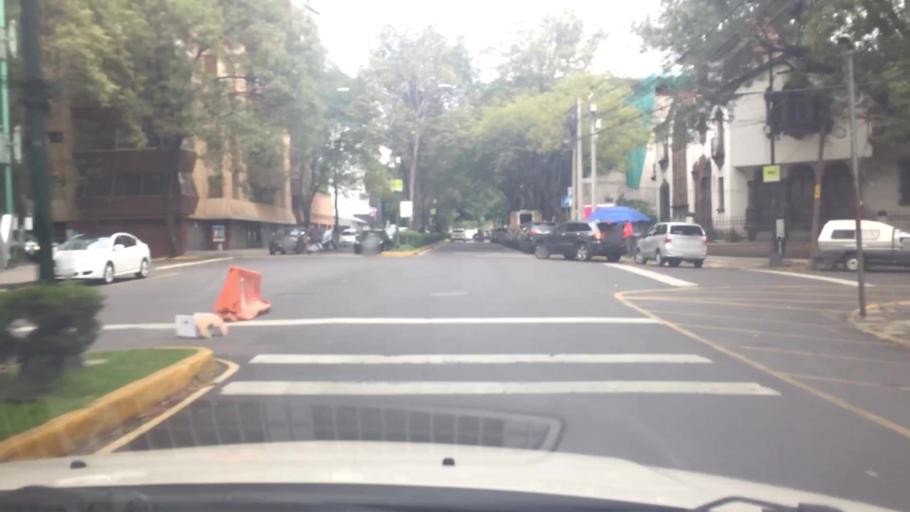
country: MX
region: Mexico City
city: Miguel Hidalgo
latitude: 19.4275
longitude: -99.1954
